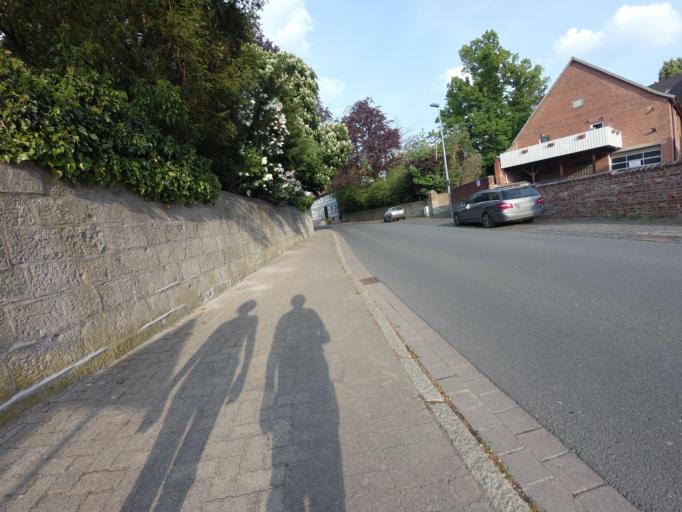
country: DE
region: Lower Saxony
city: Nordstemmen
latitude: 52.1586
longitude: 9.7786
